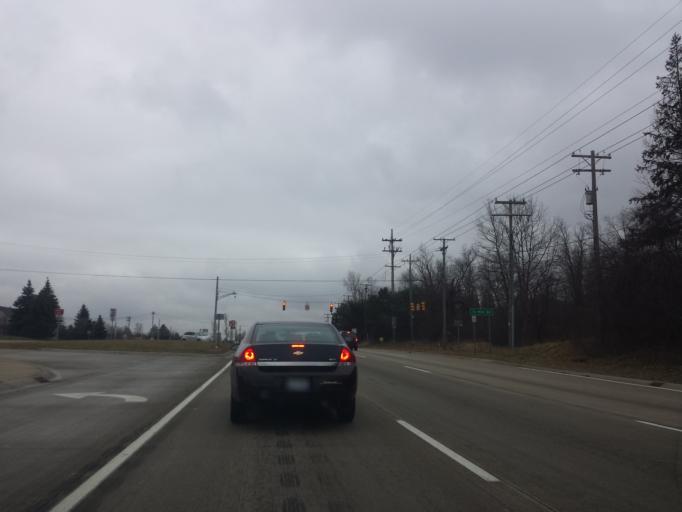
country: US
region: Michigan
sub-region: Oakland County
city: Bingham Farms
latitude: 42.5179
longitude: -83.2860
